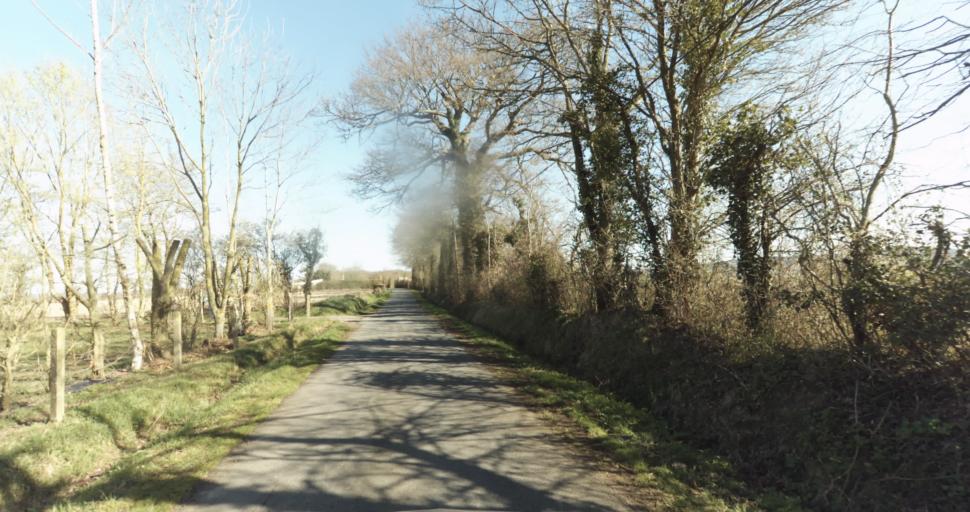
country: FR
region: Lower Normandy
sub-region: Departement du Calvados
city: Saint-Pierre-sur-Dives
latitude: 49.0457
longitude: 0.0329
